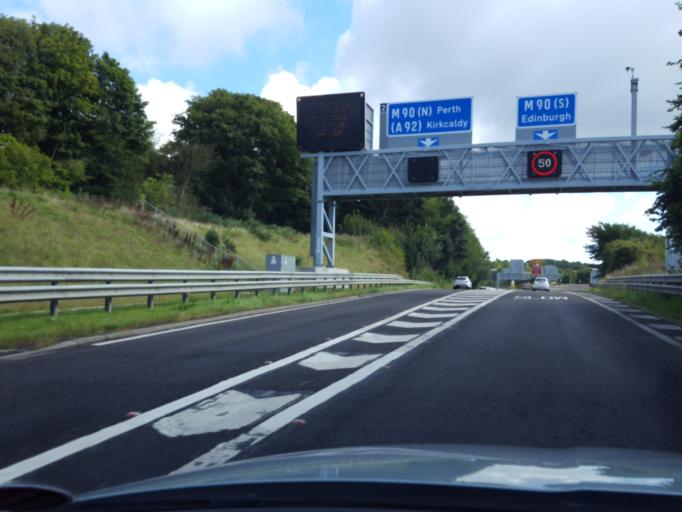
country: GB
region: Scotland
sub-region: Fife
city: Inverkeithing
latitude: 56.0454
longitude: -3.4051
